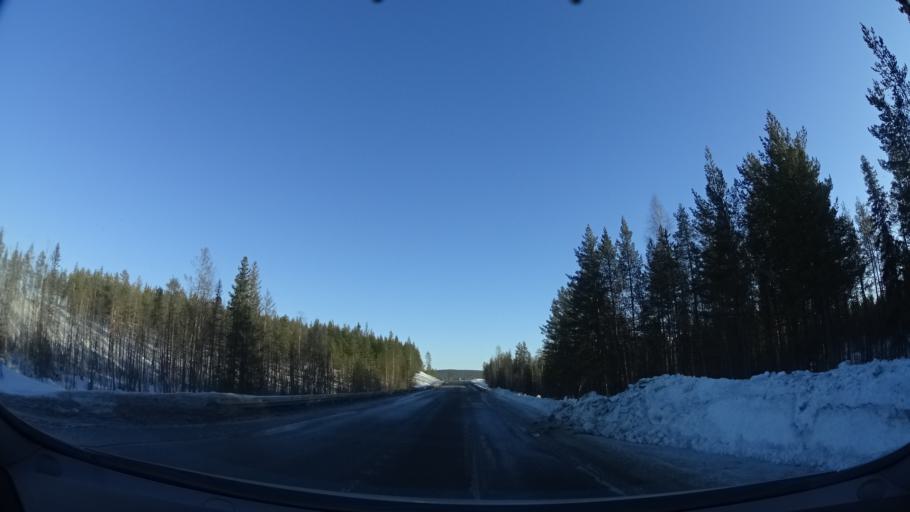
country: SE
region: Vaesterbotten
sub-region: Skelleftea Kommun
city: Langsele
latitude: 65.0413
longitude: 20.0815
